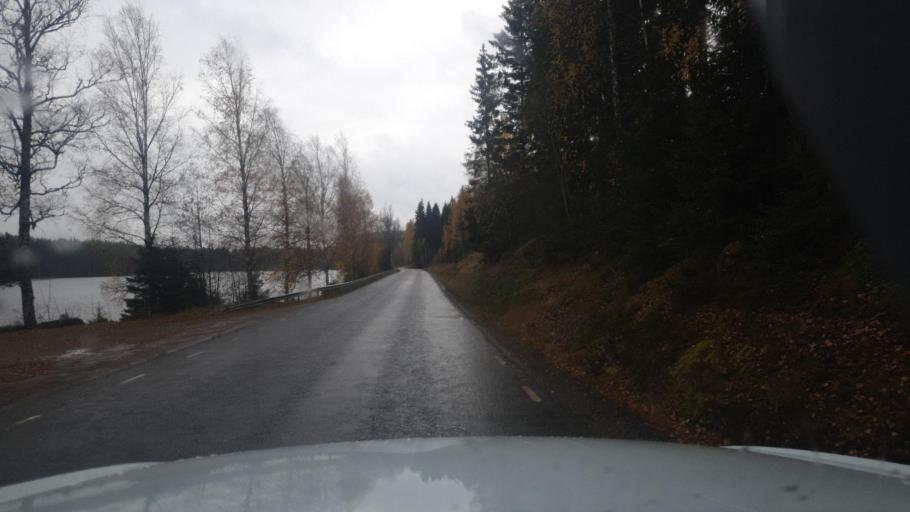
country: SE
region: Vaermland
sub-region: Eda Kommun
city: Charlottenberg
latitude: 60.0263
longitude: 12.6123
